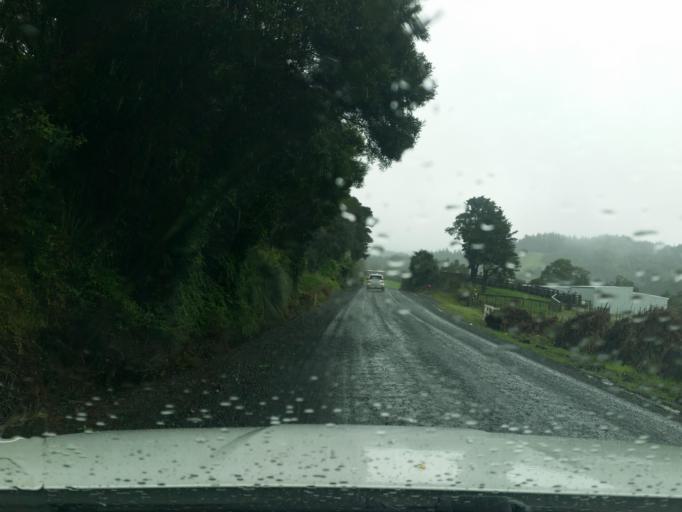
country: NZ
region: Northland
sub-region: Kaipara District
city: Dargaville
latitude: -35.8153
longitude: 174.0020
